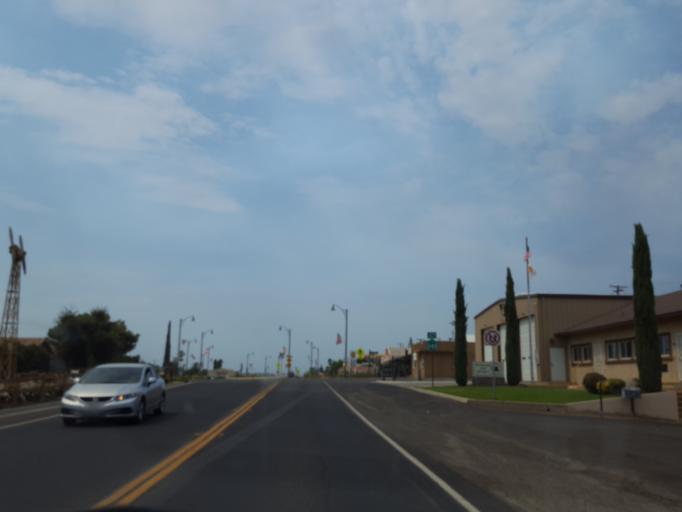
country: US
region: California
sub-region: Tulare County
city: Woodlake
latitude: 36.4138
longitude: -119.0962
